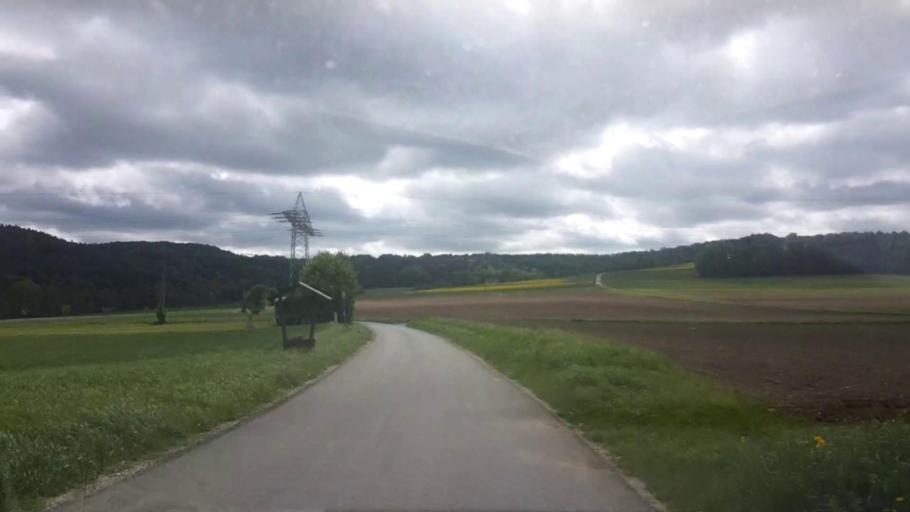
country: DE
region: Bavaria
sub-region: Upper Franconia
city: Bad Staffelstein
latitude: 50.1130
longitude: 11.0336
